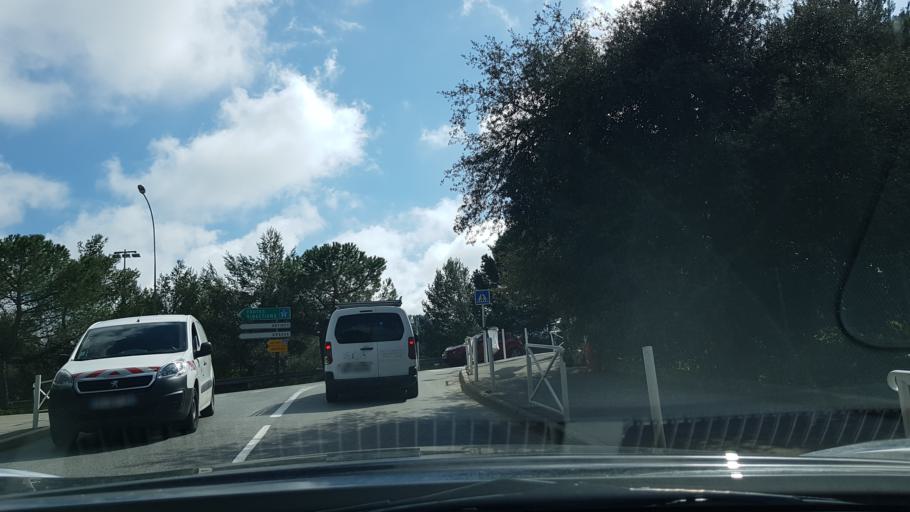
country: FR
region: Provence-Alpes-Cote d'Azur
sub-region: Departement des Alpes-Maritimes
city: Biot
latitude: 43.6035
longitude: 7.0772
